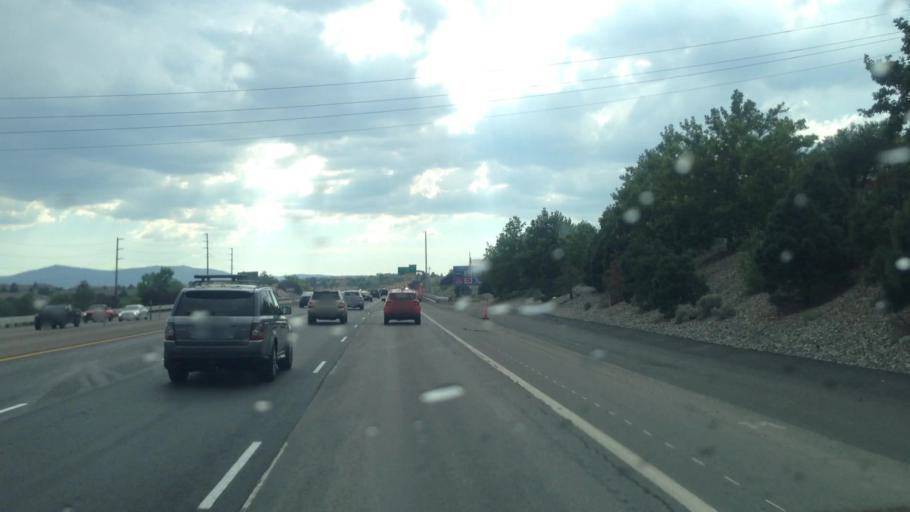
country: US
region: Nevada
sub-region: Washoe County
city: Reno
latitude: 39.5269
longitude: -119.8490
